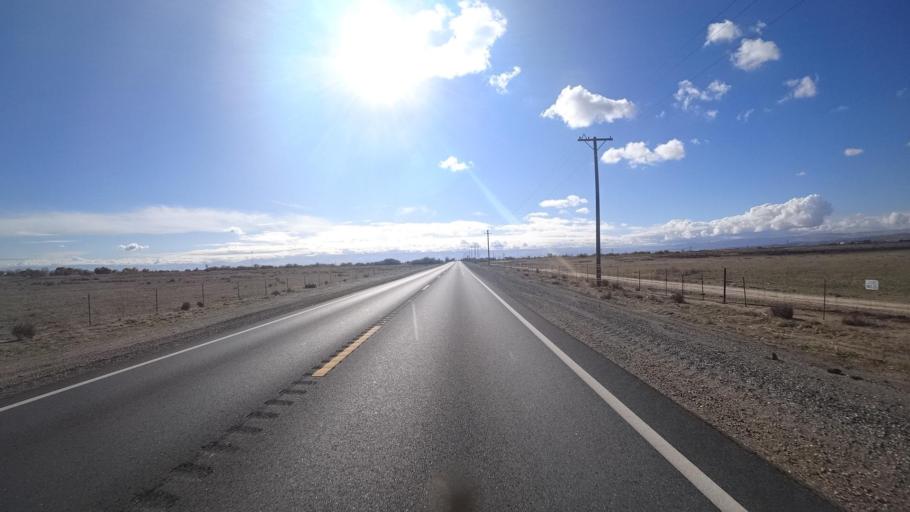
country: US
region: California
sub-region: Kern County
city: Rosedale
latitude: 35.3098
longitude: -119.2526
